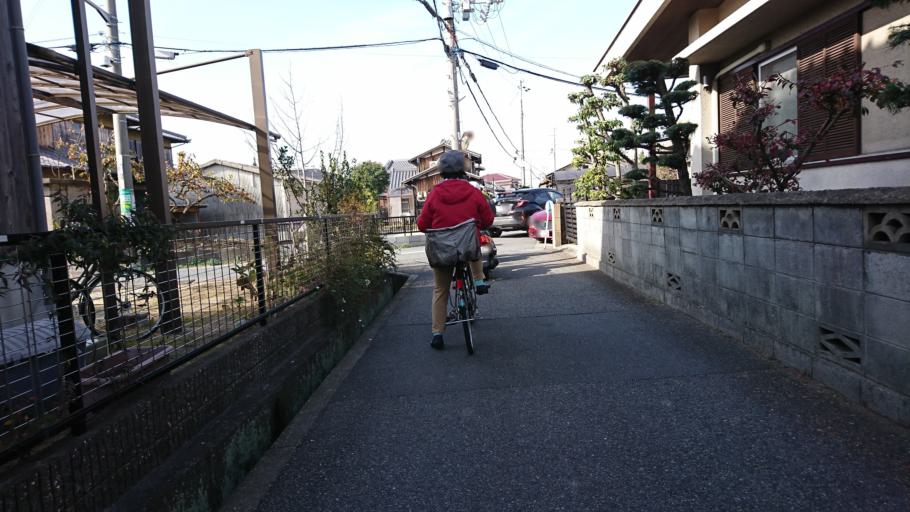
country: JP
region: Hyogo
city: Kakogawacho-honmachi
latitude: 34.7478
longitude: 134.8468
